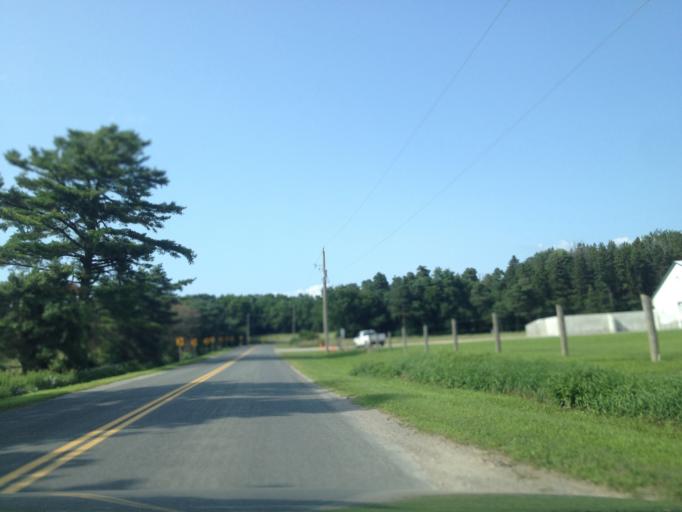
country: CA
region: Ontario
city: Aylmer
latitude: 42.7442
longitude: -80.8532
